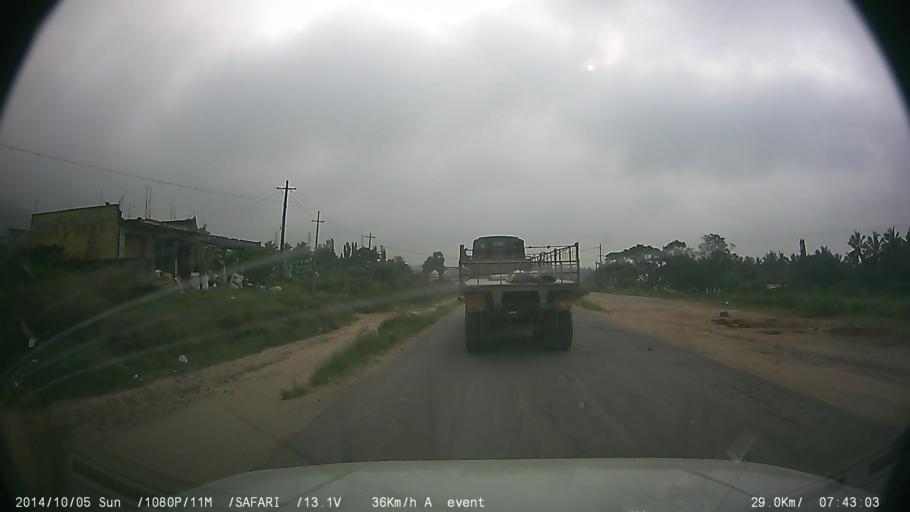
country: IN
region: Tamil Nadu
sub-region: Coimbatore
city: Madukkarai
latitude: 10.8938
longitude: 76.9263
